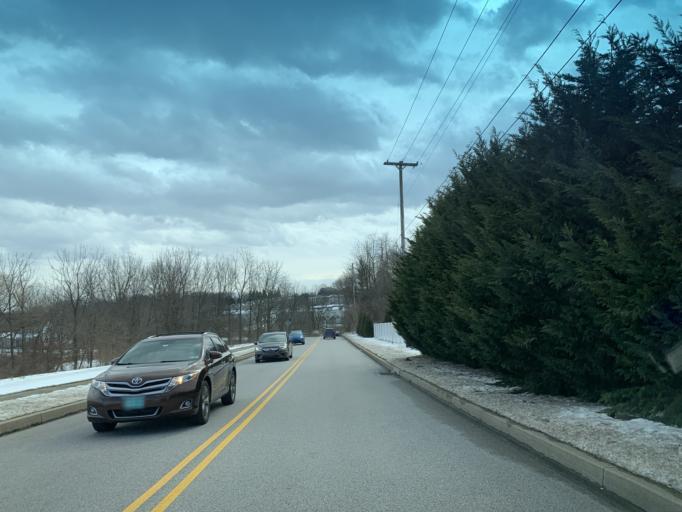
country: US
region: Pennsylvania
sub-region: York County
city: Shrewsbury
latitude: 39.7633
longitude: -76.6729
